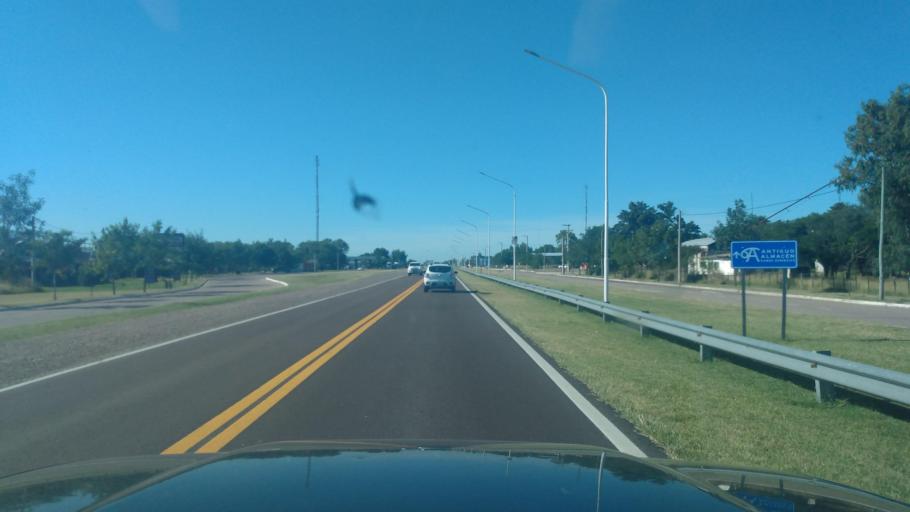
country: AR
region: La Pampa
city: Doblas
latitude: -37.0278
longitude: -64.2889
